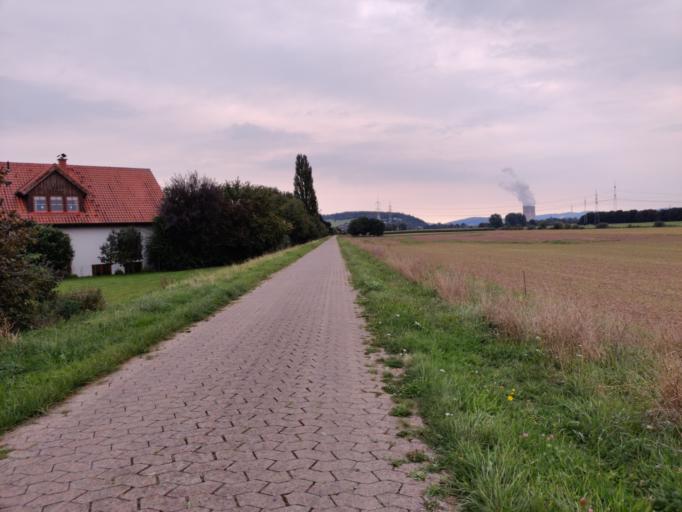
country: DE
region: Lower Saxony
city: Hameln
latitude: 52.0626
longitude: 9.3703
